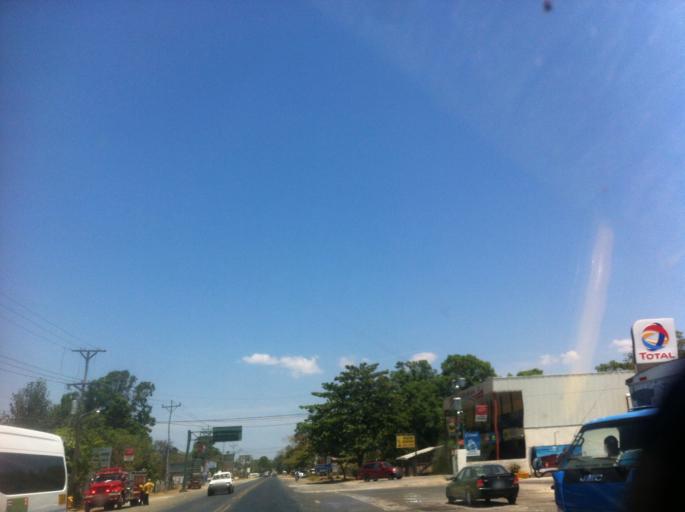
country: CR
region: Guanacaste
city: Sardinal
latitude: 10.5420
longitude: -85.5878
